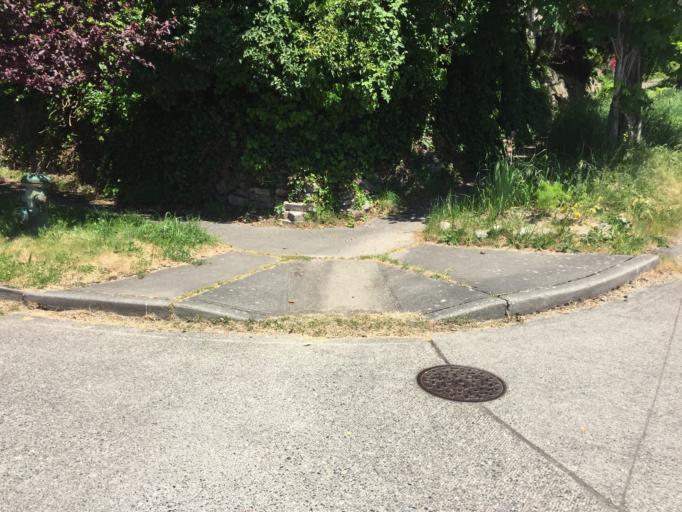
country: US
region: Washington
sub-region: King County
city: Seattle
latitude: 47.5913
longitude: -122.2934
